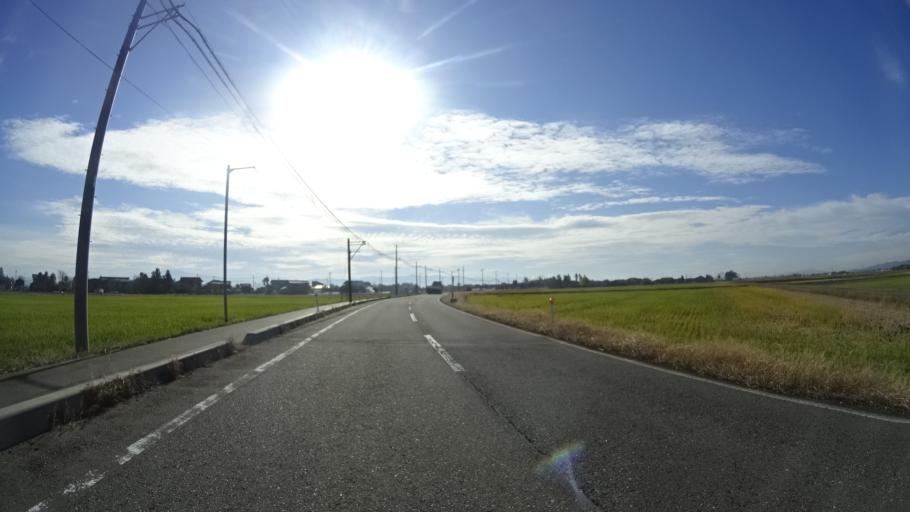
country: JP
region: Niigata
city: Mitsuke
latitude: 37.5634
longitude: 138.8487
